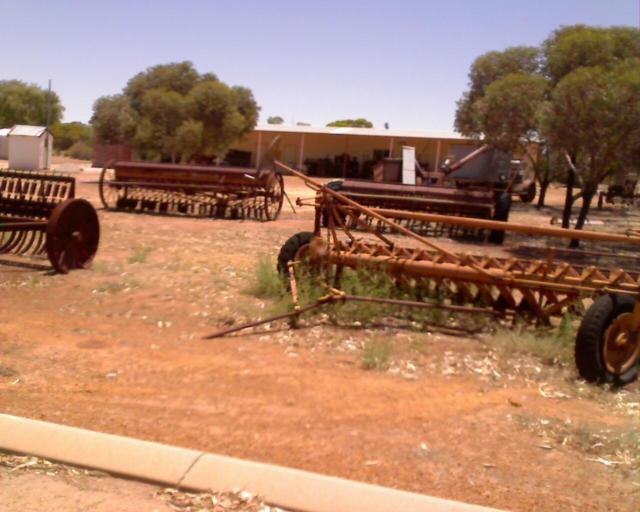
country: AU
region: Western Australia
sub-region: Wongan-Ballidu
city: Wongan Hills
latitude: -30.8266
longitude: 117.4866
